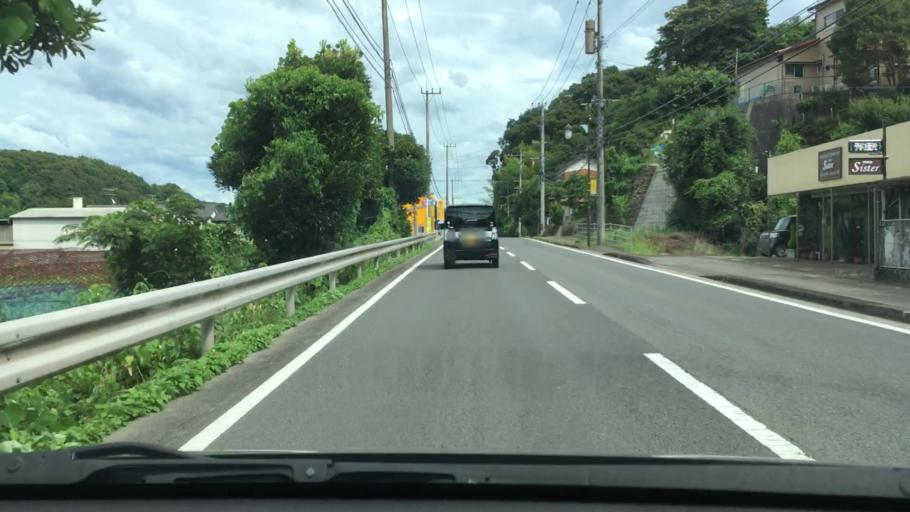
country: JP
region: Nagasaki
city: Togitsu
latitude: 32.8904
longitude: 129.7835
